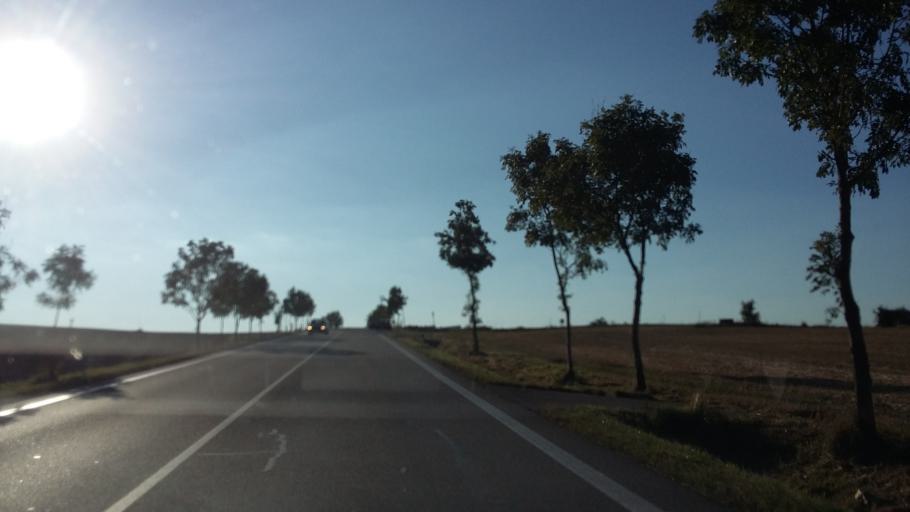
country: CZ
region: Vysocina
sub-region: Okres Zd'ar nad Sazavou
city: Velke Mezirici
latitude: 49.3746
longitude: 15.9537
